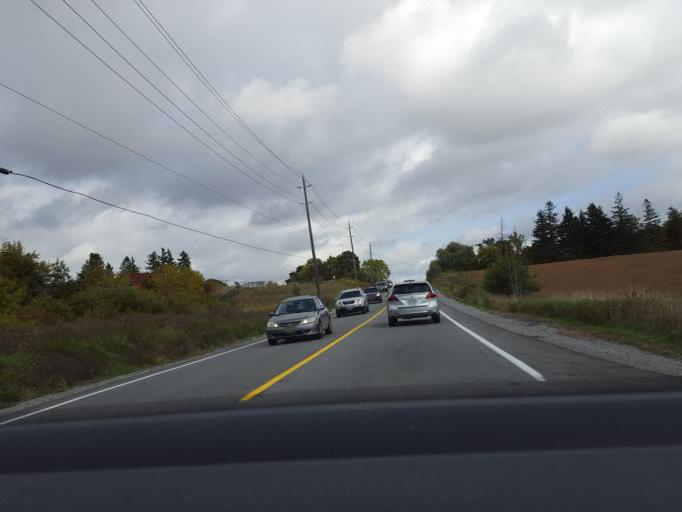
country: CA
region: Ontario
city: Pickering
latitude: 43.8507
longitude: -79.1899
